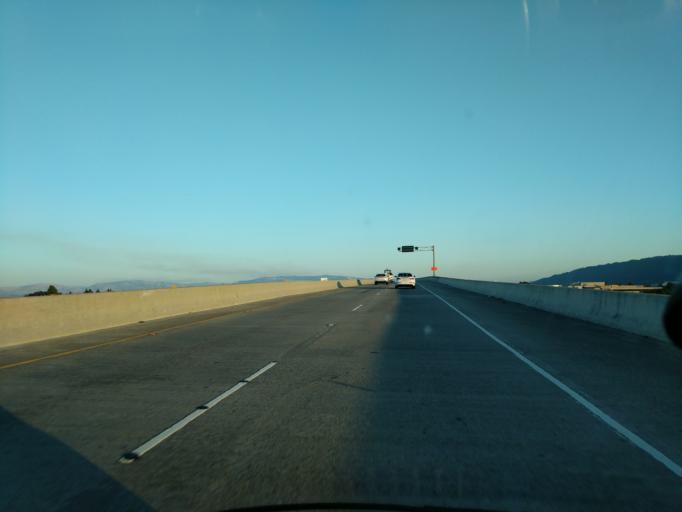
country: US
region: California
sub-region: Alameda County
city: Dublin
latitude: 37.7046
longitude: -121.9251
